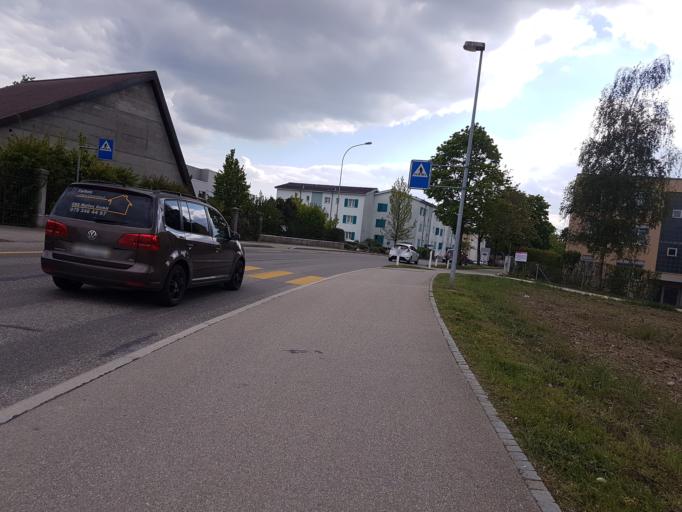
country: CH
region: Bern
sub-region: Biel/Bienne District
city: Orpund
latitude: 47.1413
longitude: 7.3153
